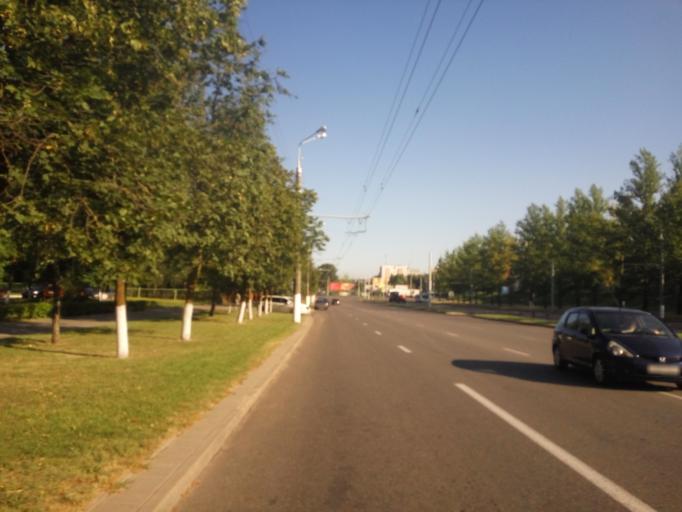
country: BY
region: Vitebsk
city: Vitebsk
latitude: 55.1937
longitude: 30.2494
